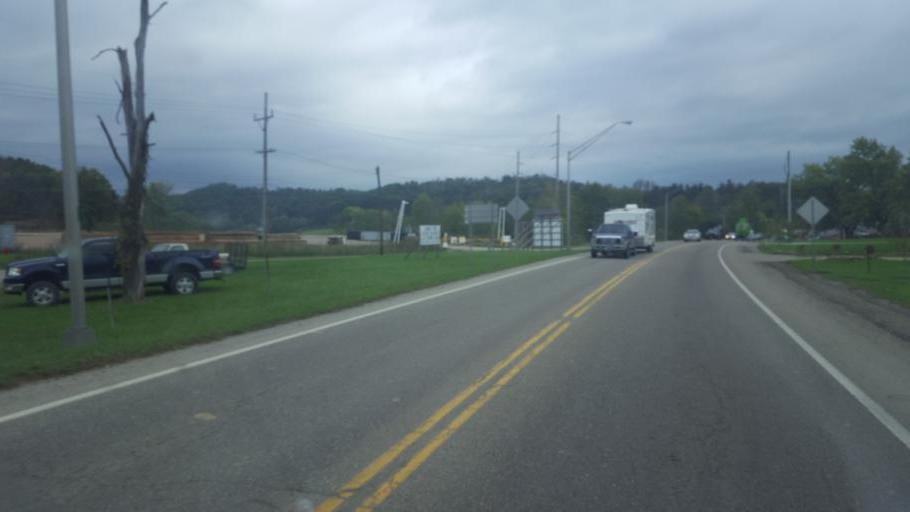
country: US
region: Ohio
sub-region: Tuscarawas County
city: Dennison
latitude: 40.4018
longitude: -81.3242
